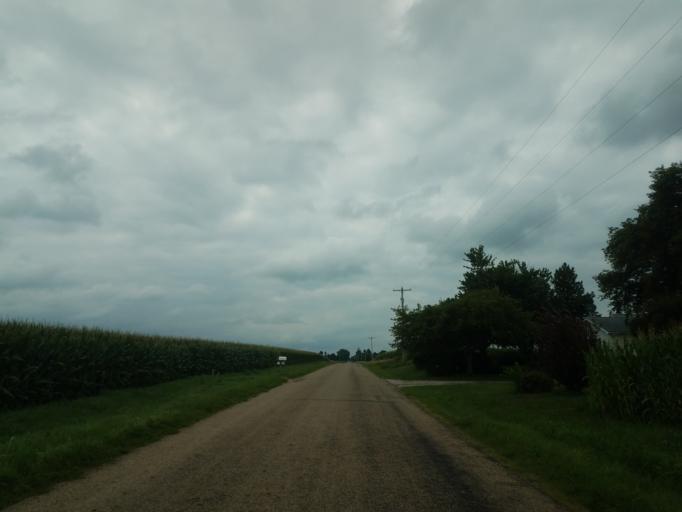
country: US
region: Illinois
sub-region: McLean County
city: Twin Grove
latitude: 40.4227
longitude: -89.0621
